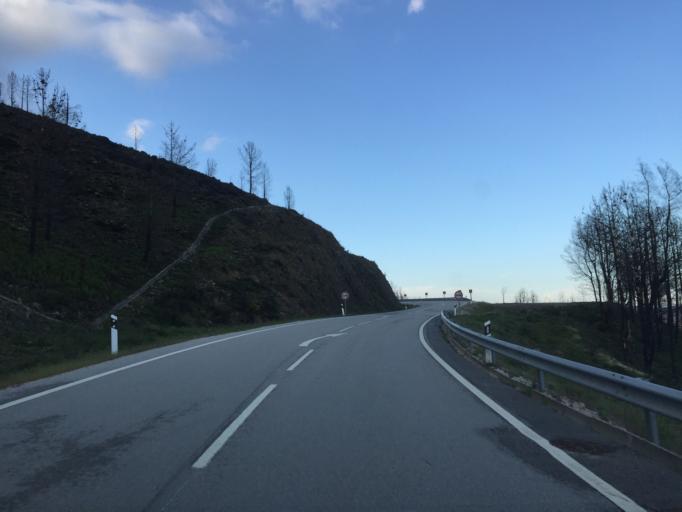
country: PT
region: Coimbra
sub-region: Gois
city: Gois
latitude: 40.0969
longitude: -8.0522
